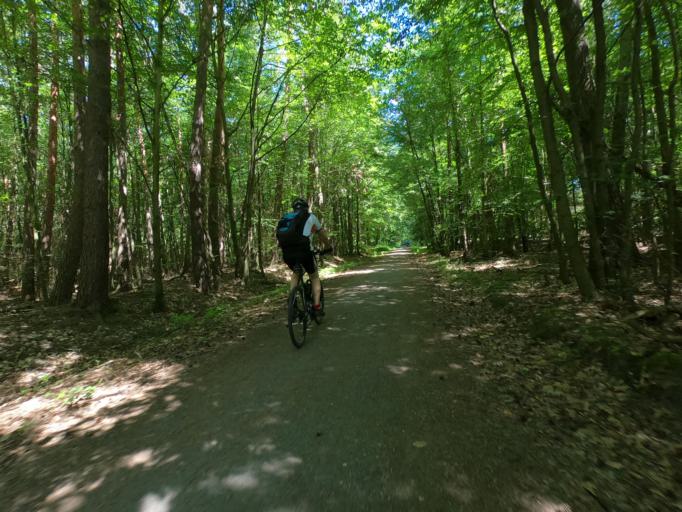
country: DE
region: Hesse
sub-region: Regierungsbezirk Darmstadt
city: Dietzenbach
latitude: 50.0313
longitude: 8.7739
